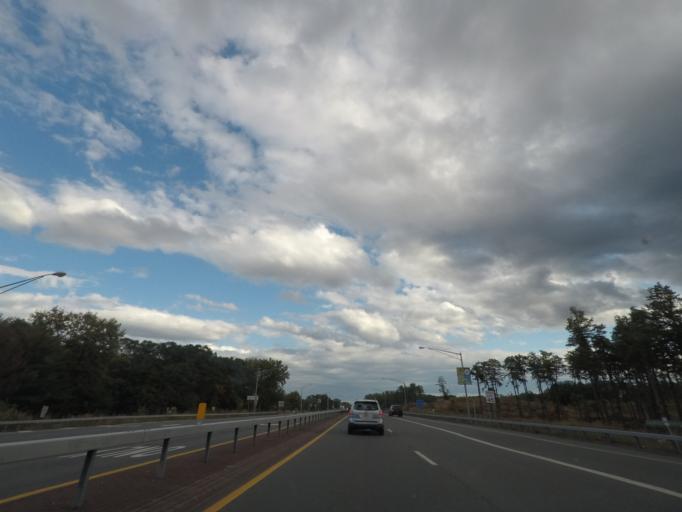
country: US
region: New York
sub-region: Albany County
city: Westmere
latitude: 42.7123
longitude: -73.8709
